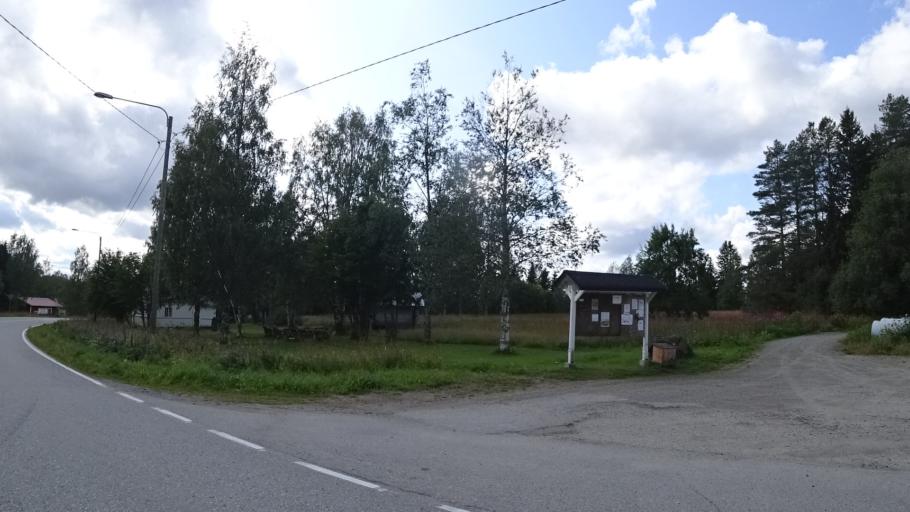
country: FI
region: North Karelia
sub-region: Joensuu
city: Ilomantsi
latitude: 62.9326
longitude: 31.2823
